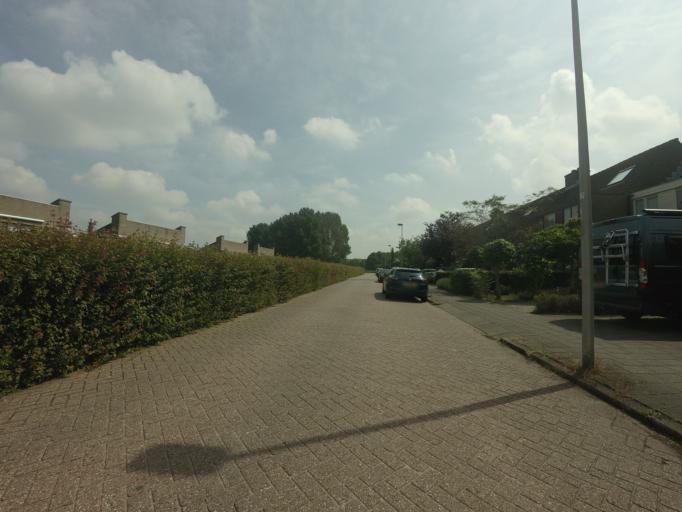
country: NL
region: Utrecht
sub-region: Gemeente Vianen
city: Vianen
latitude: 52.0038
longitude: 5.0893
